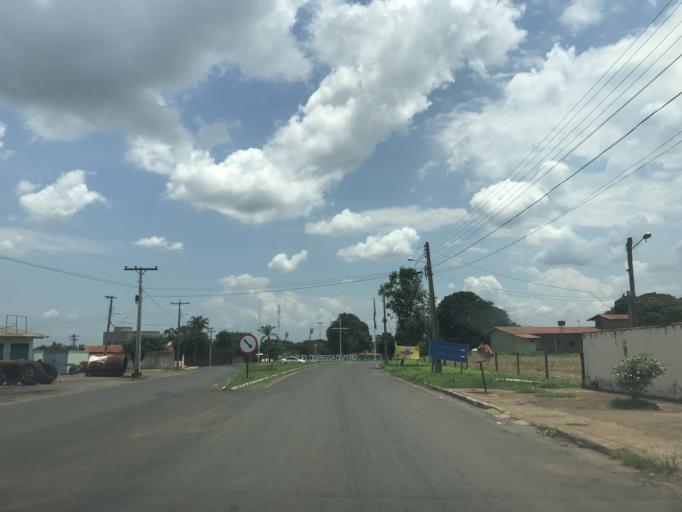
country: BR
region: Goias
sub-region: Bela Vista De Goias
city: Bela Vista de Goias
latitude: -17.0498
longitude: -48.6649
